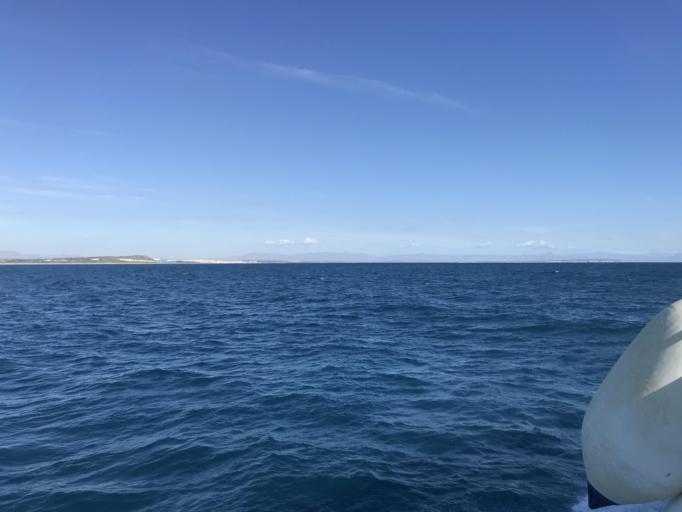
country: ES
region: Valencia
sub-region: Provincia de Alicante
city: Torrevieja
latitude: 38.0114
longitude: -0.6287
